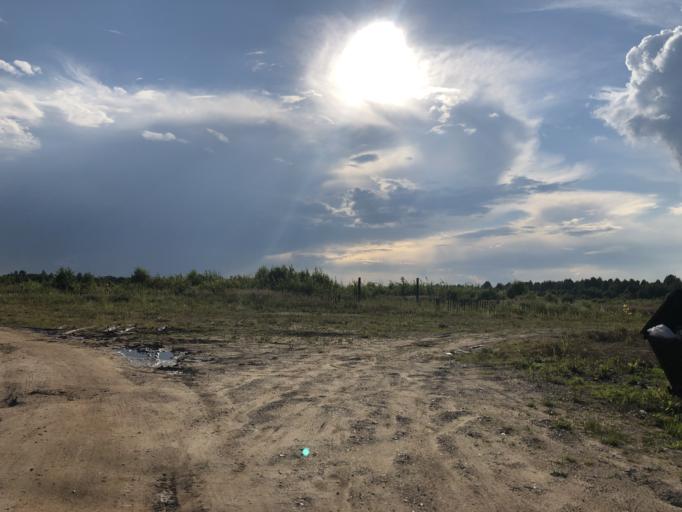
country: RU
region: Tverskaya
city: Rzhev
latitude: 56.2674
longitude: 34.2425
